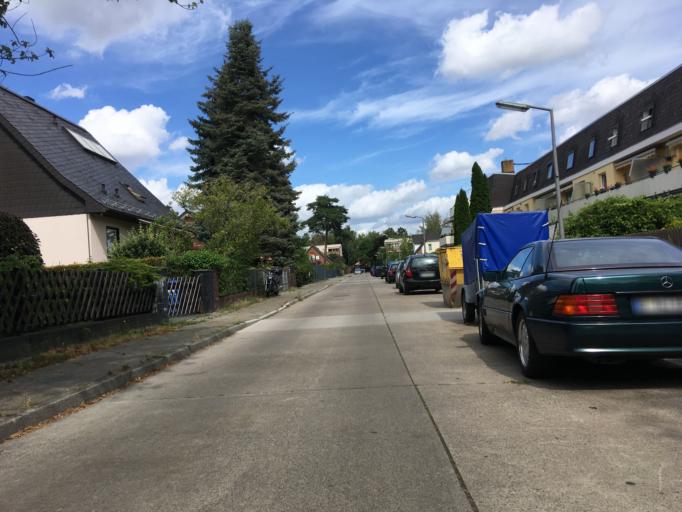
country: DE
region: Berlin
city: Mariendorf
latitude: 52.4354
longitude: 13.4031
